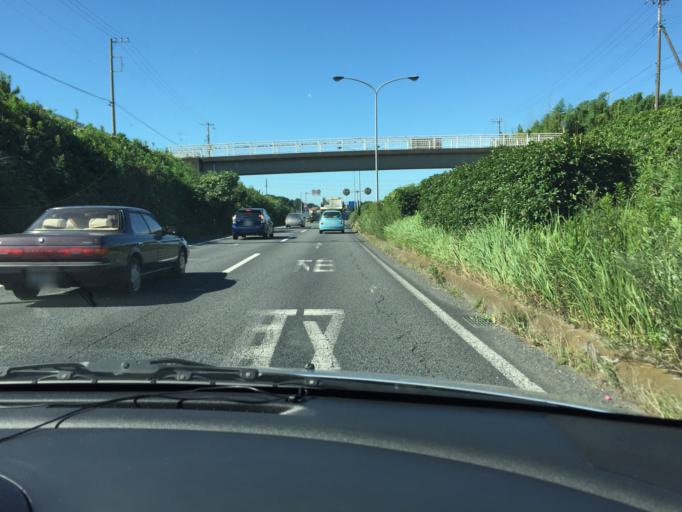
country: JP
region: Ibaraki
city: Naka
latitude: 36.0610
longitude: 140.1784
